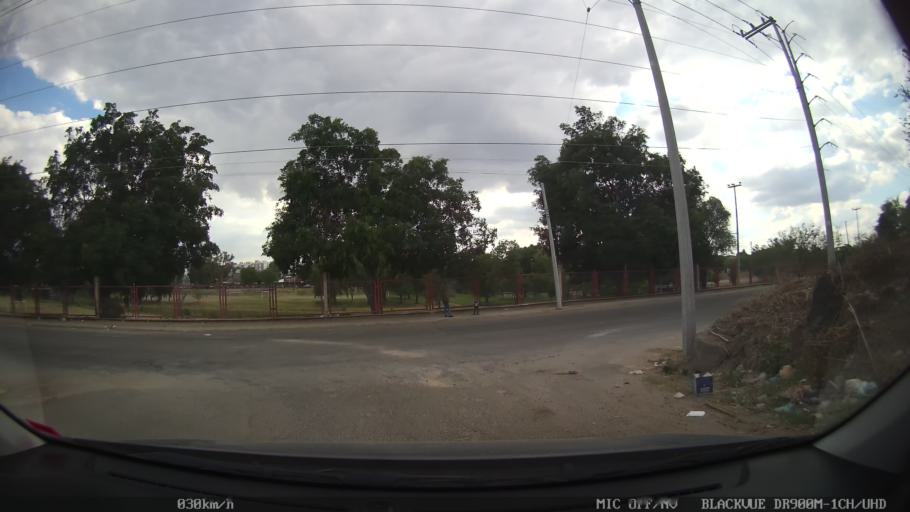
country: MX
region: Jalisco
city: Tlaquepaque
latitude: 20.6594
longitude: -103.2676
